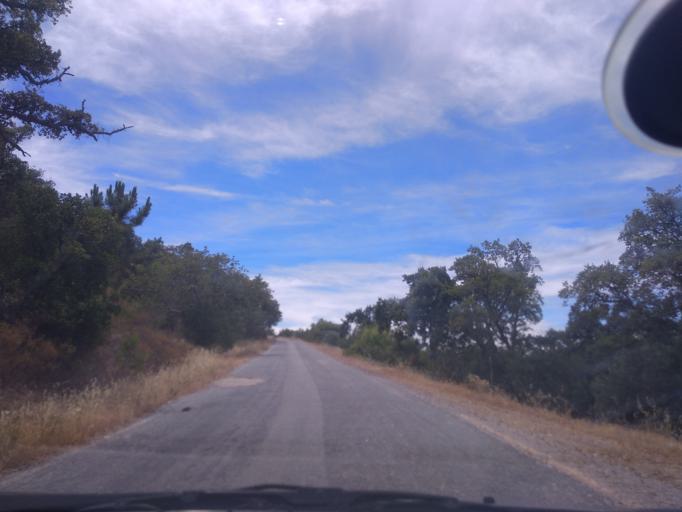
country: PT
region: Faro
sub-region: Sao Bras de Alportel
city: Sao Bras de Alportel
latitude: 37.1783
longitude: -7.8044
